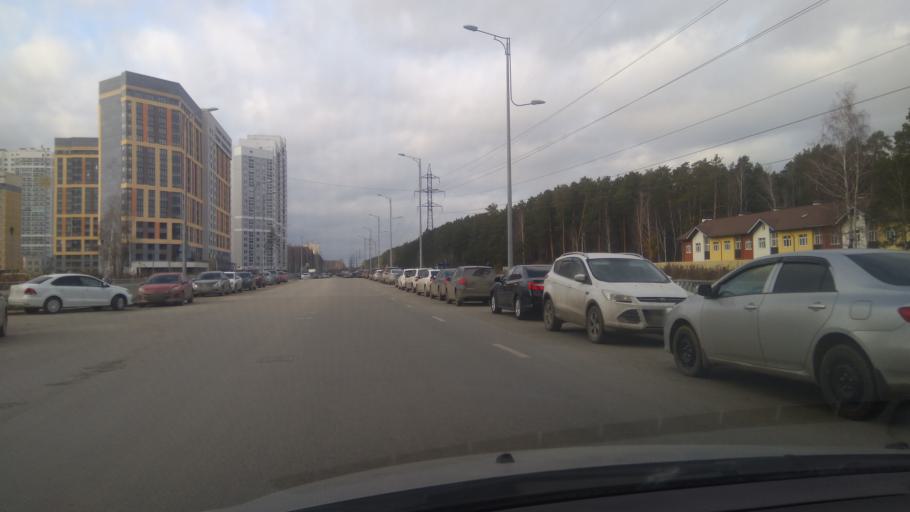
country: RU
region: Sverdlovsk
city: Sovkhoznyy
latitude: 56.7838
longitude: 60.5527
